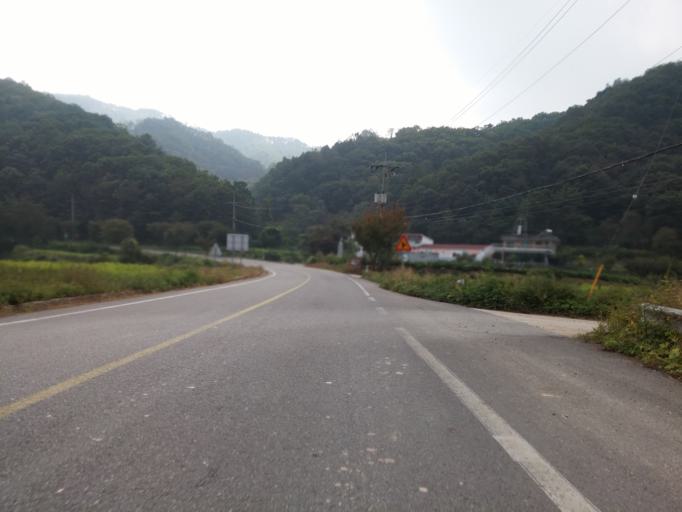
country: KR
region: Chungcheongbuk-do
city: Yong-dong
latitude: 36.3669
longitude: 127.8112
